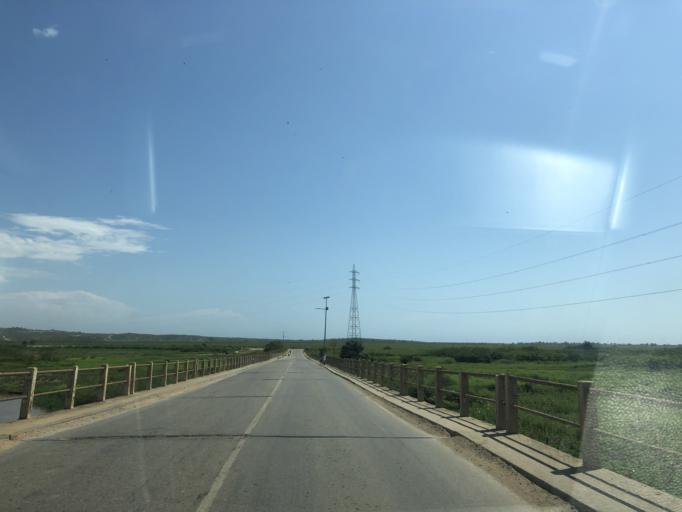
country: AO
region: Cuanza Sul
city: Sumbe
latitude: -10.8740
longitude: 13.8404
